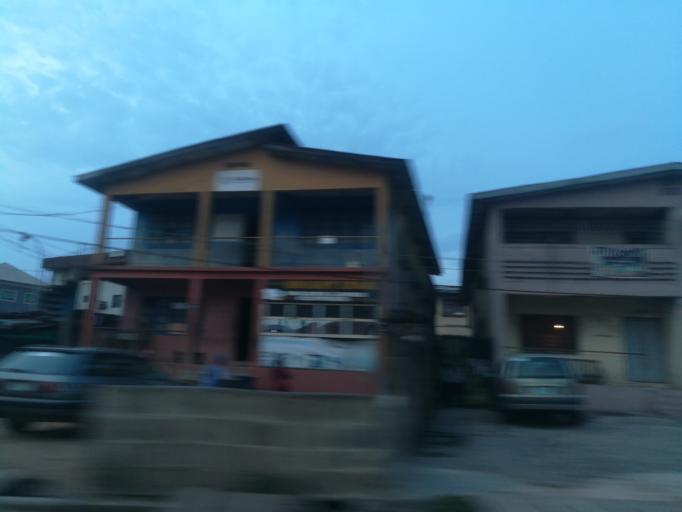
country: NG
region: Oyo
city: Ibadan
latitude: 7.3922
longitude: 3.9037
